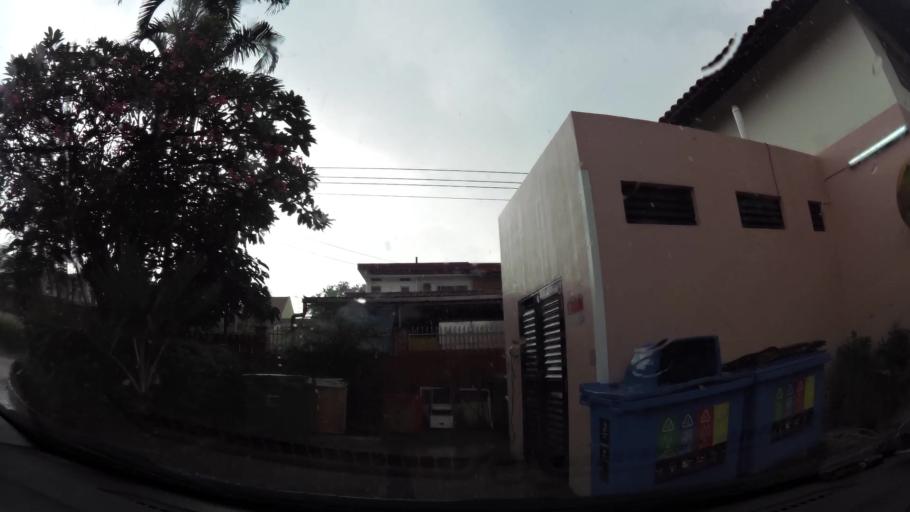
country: SG
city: Singapore
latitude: 1.3328
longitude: 103.9489
